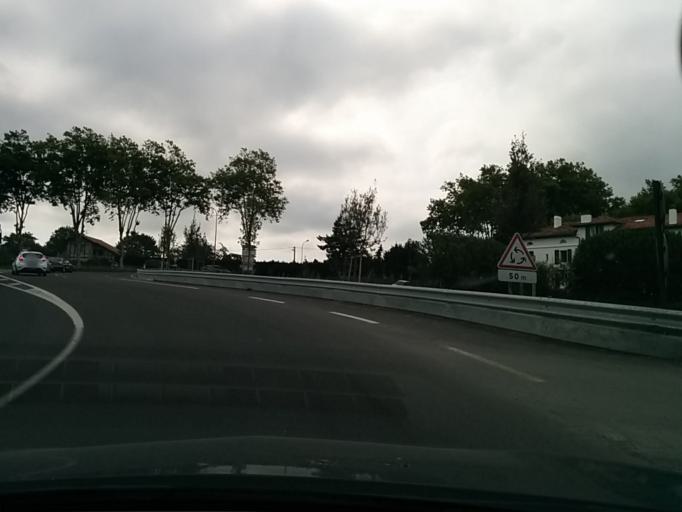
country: FR
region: Aquitaine
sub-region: Departement des Pyrenees-Atlantiques
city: Ciboure
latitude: 43.3727
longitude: -1.6824
